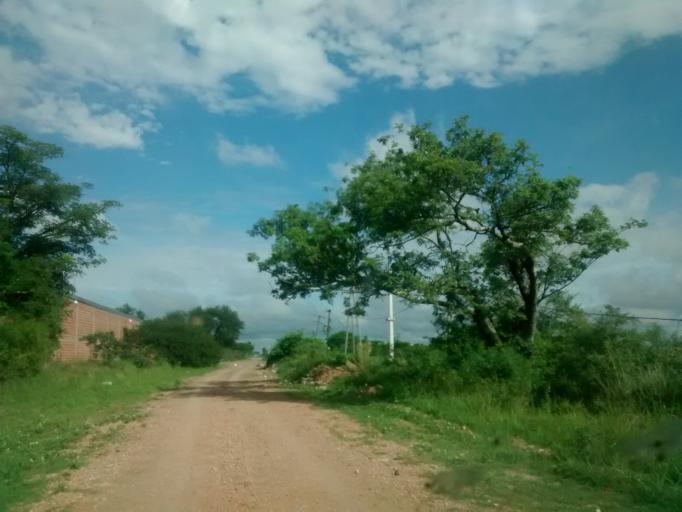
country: AR
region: Chaco
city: Fontana
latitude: -27.4070
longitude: -58.9789
